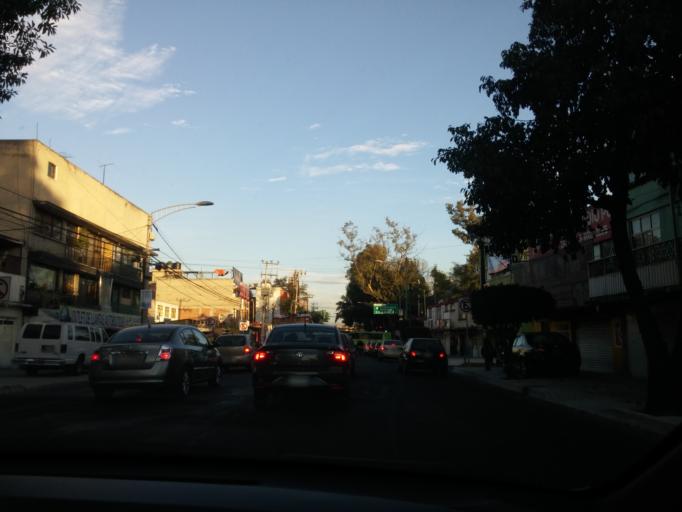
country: MX
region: Mexico City
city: Cuauhtemoc
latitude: 19.4564
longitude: -99.1669
